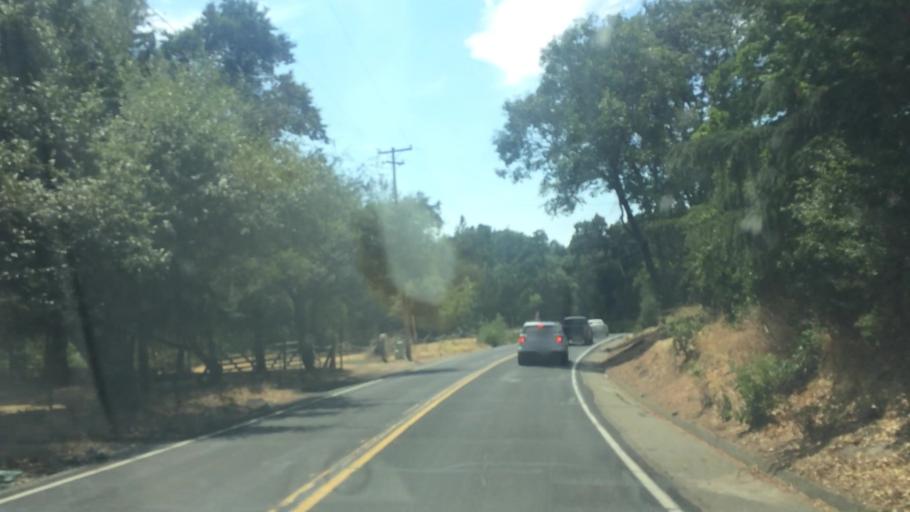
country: US
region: California
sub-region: Amador County
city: Pine Grove
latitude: 38.4104
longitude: -120.7072
